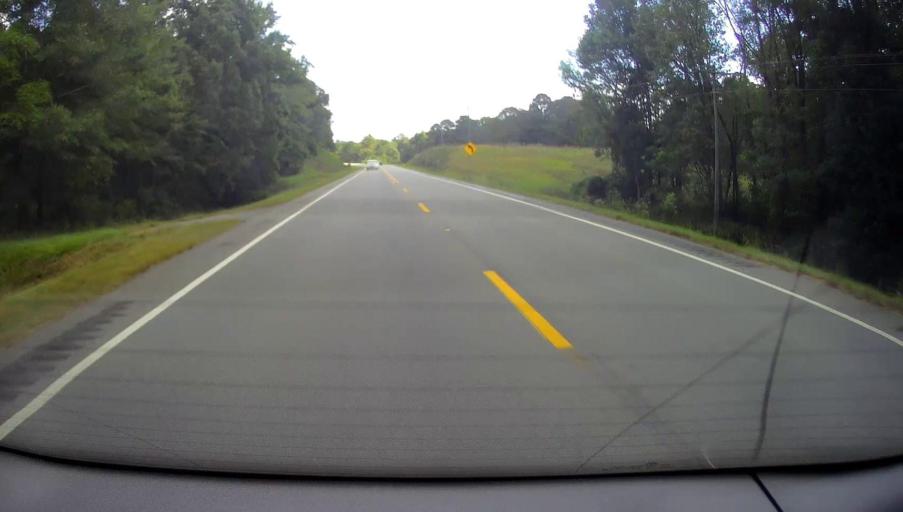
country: US
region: Georgia
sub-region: Baldwin County
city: Milledgeville
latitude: 33.0738
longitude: -83.3258
